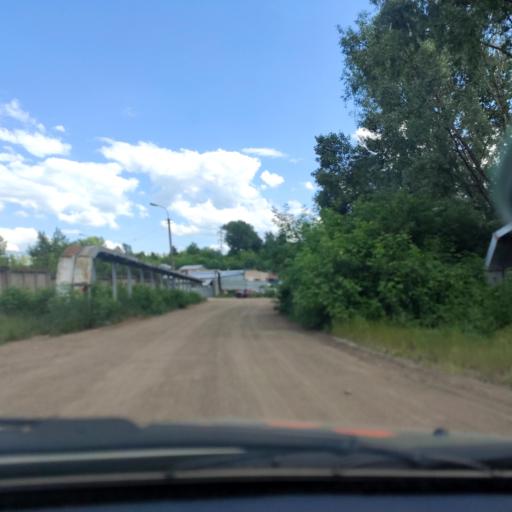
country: RU
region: Bashkortostan
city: Ufa
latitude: 54.8341
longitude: 56.0634
